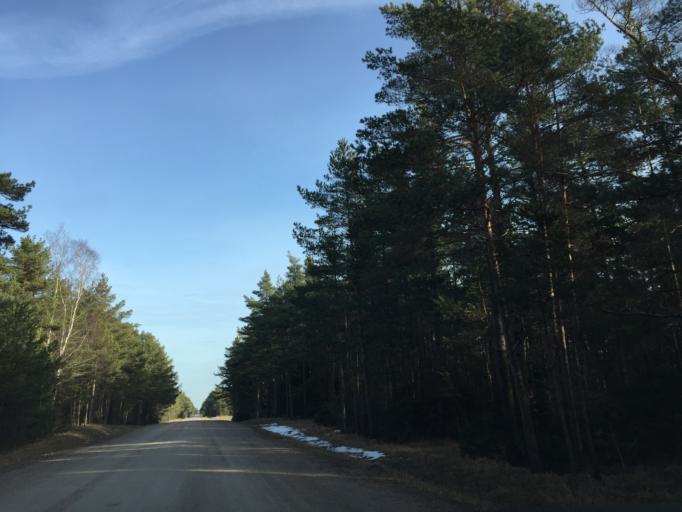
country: EE
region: Saare
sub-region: Kuressaare linn
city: Kuressaare
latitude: 58.2994
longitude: 21.9553
